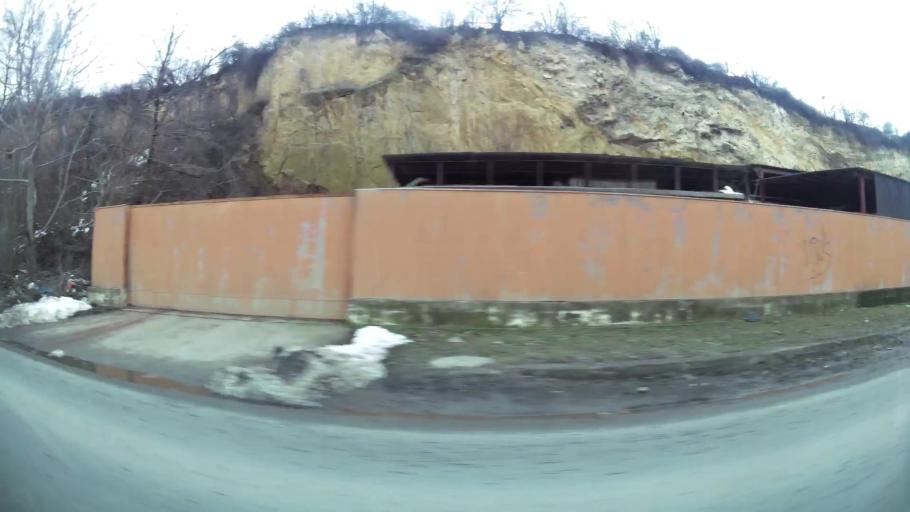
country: RS
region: Central Serbia
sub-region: Belgrade
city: Cukarica
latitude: 44.7587
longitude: 20.4034
